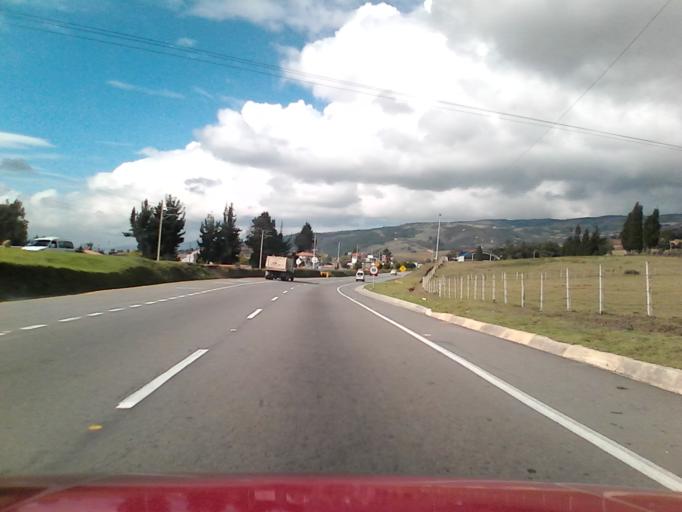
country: CO
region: Boyaca
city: Combita
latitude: 5.6276
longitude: -73.3039
